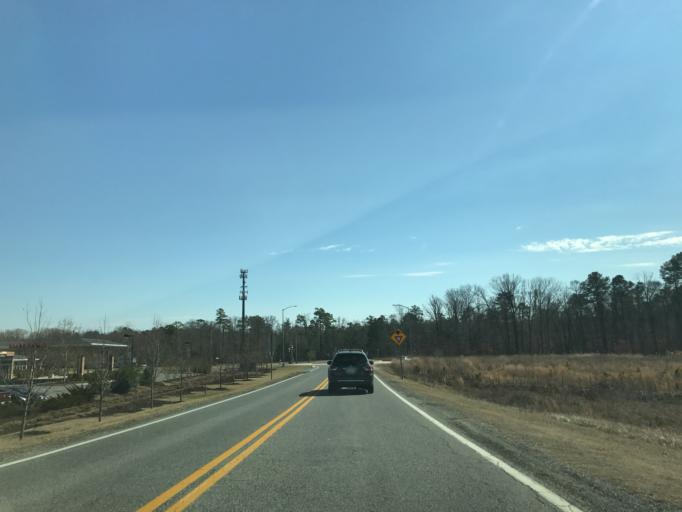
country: US
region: Maryland
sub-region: Queen Anne's County
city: Grasonville
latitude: 38.9670
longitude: -76.1840
